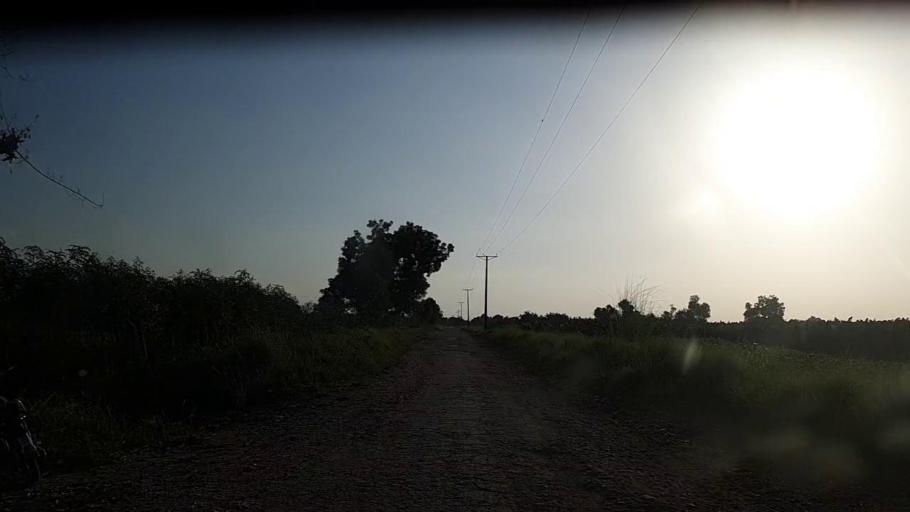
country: PK
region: Sindh
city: Hingorja
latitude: 27.0593
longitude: 68.4129
